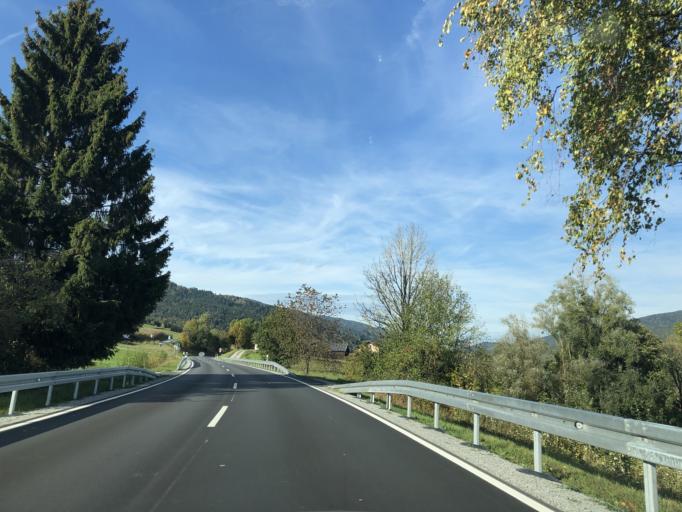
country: DE
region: Bavaria
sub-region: Lower Bavaria
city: Deggendorf
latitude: 48.8657
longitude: 12.9590
